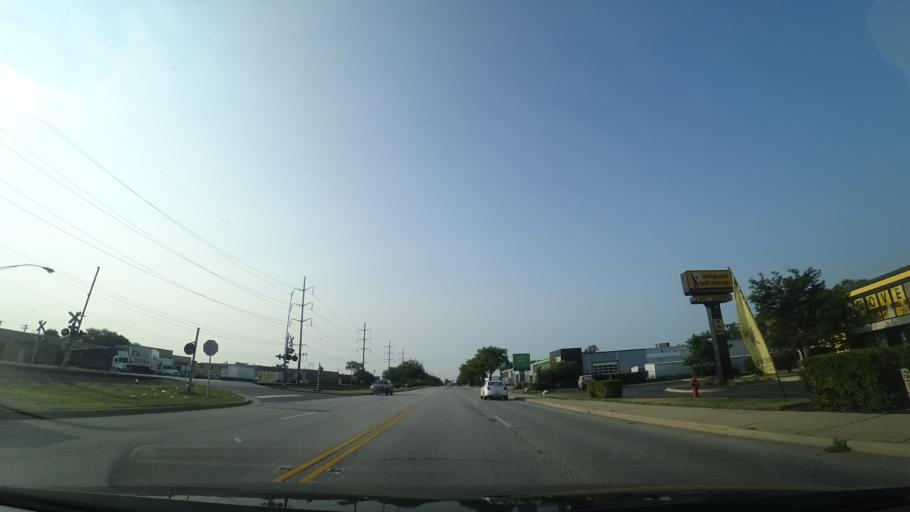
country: US
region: Illinois
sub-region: Cook County
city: Des Plaines
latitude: 42.0161
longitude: -87.8882
